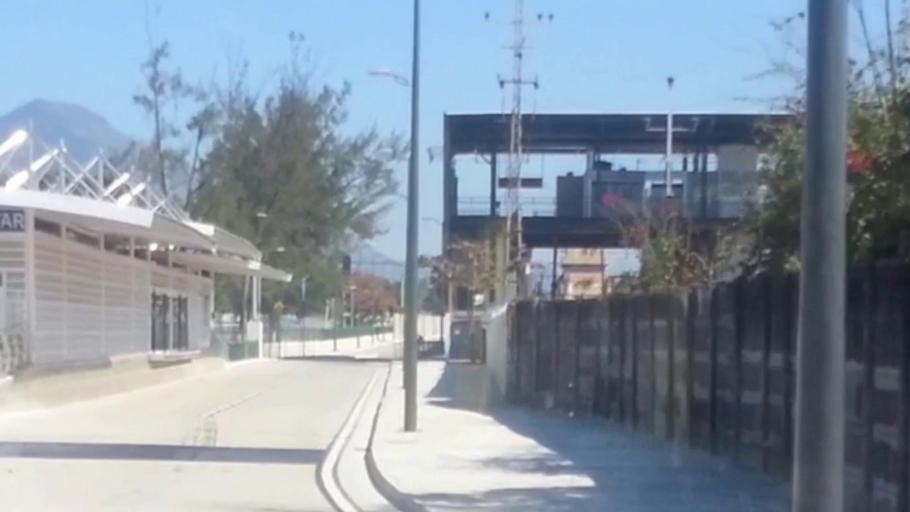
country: BR
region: Rio de Janeiro
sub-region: Nilopolis
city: Nilopolis
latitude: -22.8608
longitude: -43.3980
